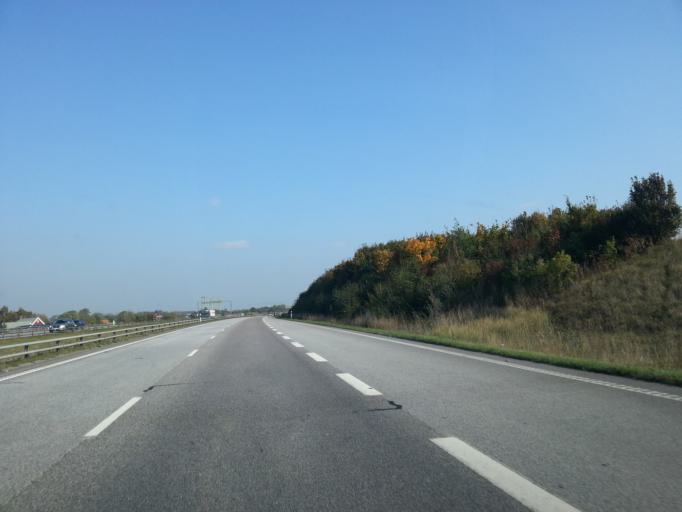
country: SE
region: Skane
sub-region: Malmo
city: Oxie
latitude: 55.5656
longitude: 13.0864
